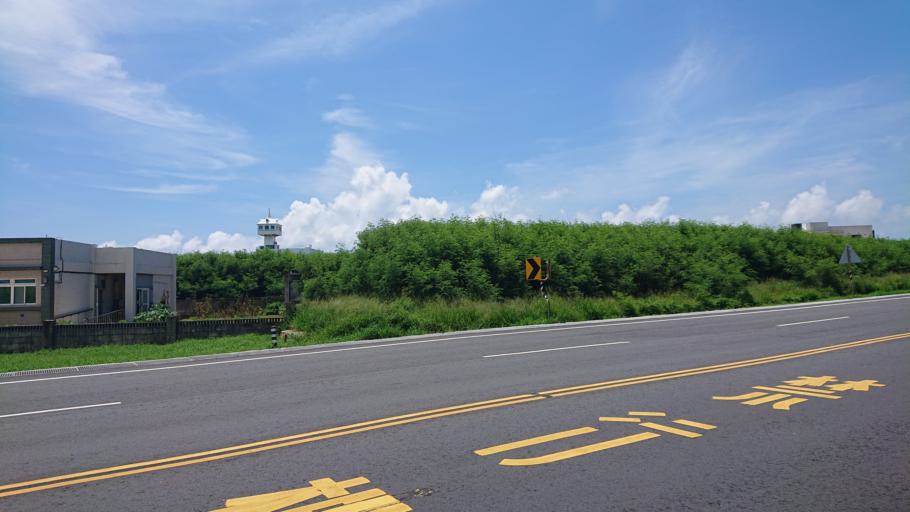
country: TW
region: Taiwan
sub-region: Penghu
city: Ma-kung
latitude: 23.6144
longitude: 119.6077
